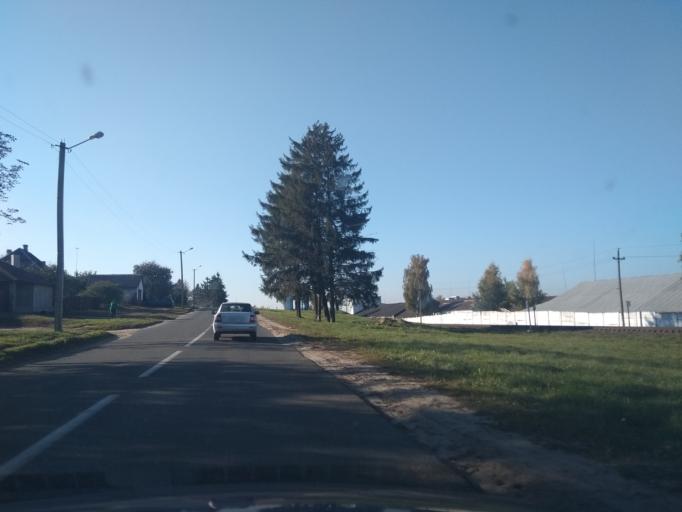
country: BY
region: Grodnenskaya
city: Vawkavysk
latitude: 53.1559
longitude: 24.4641
